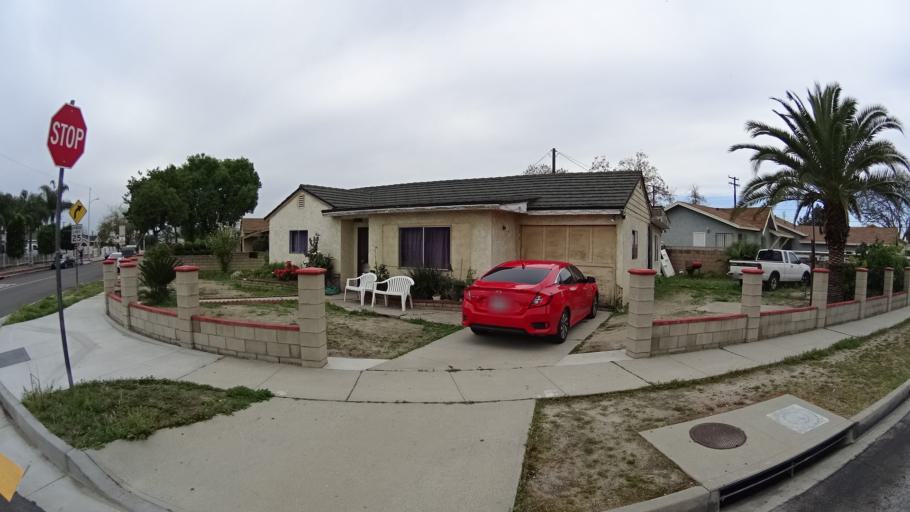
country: US
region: California
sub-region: Los Angeles County
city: West Puente Valley
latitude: 34.0736
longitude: -117.9895
